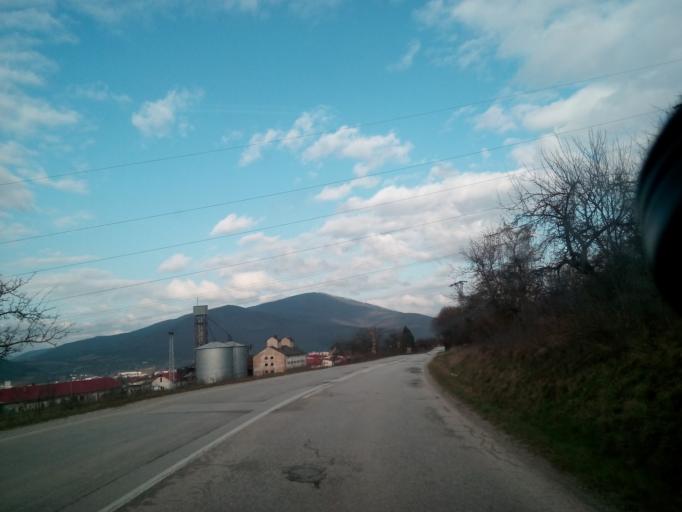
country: SK
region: Kosicky
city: Roznava
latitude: 48.6533
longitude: 20.5544
